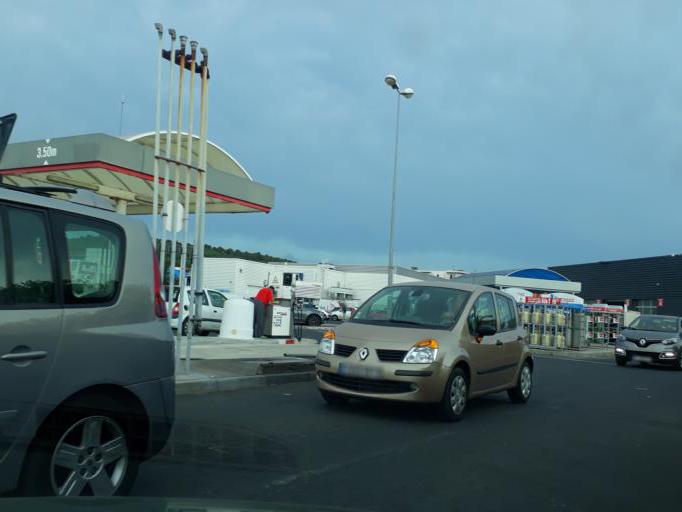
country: FR
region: Languedoc-Roussillon
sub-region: Departement de l'Herault
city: Agde
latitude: 43.3069
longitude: 3.4913
